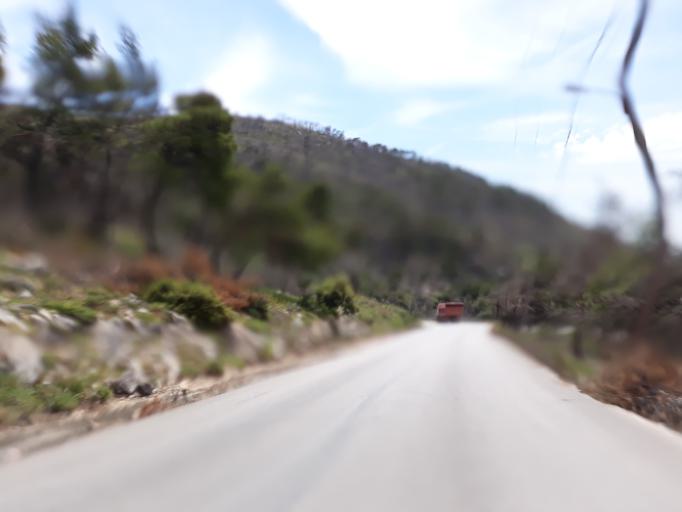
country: GR
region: Attica
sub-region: Nomarchia Dytikis Attikis
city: Magoula
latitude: 38.1581
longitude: 23.5306
